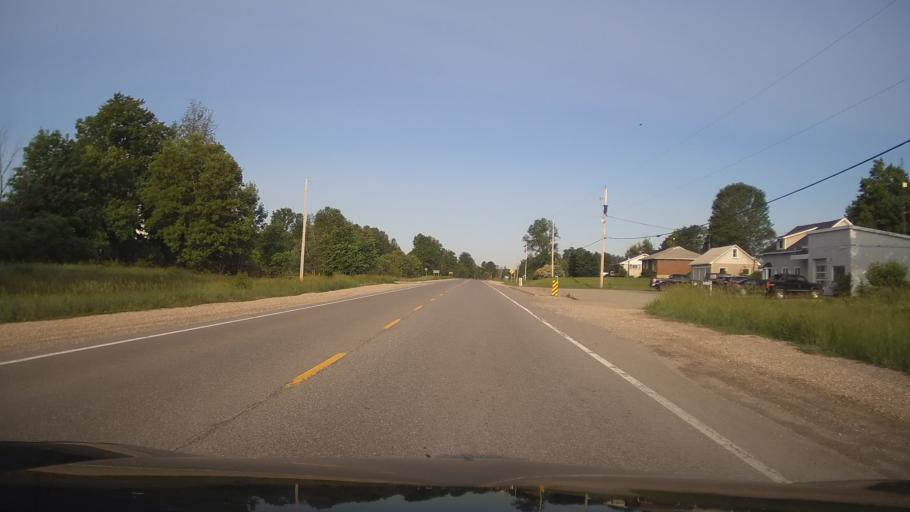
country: CA
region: Ontario
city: Perth
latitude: 44.8695
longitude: -76.3836
